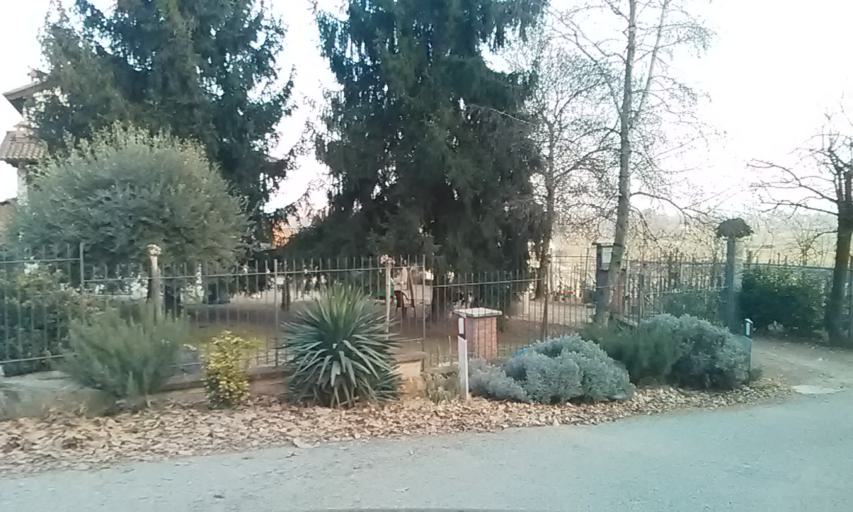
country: IT
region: Piedmont
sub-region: Provincia di Biella
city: Dorzano
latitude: 45.4167
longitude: 8.1126
